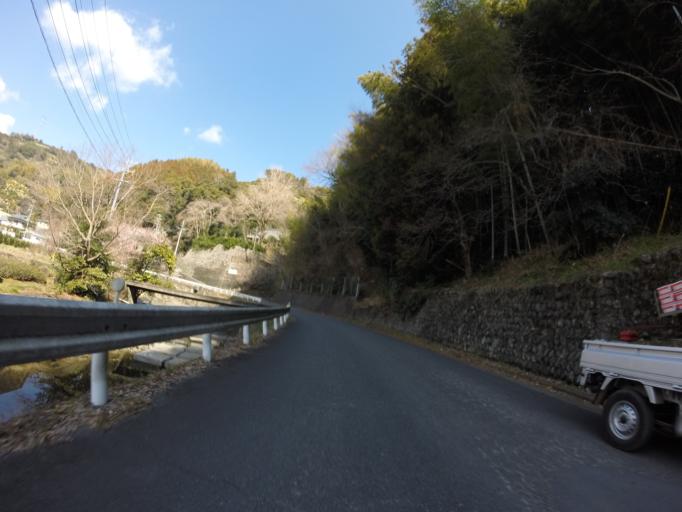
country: JP
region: Shizuoka
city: Shizuoka-shi
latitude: 35.0735
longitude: 138.4851
